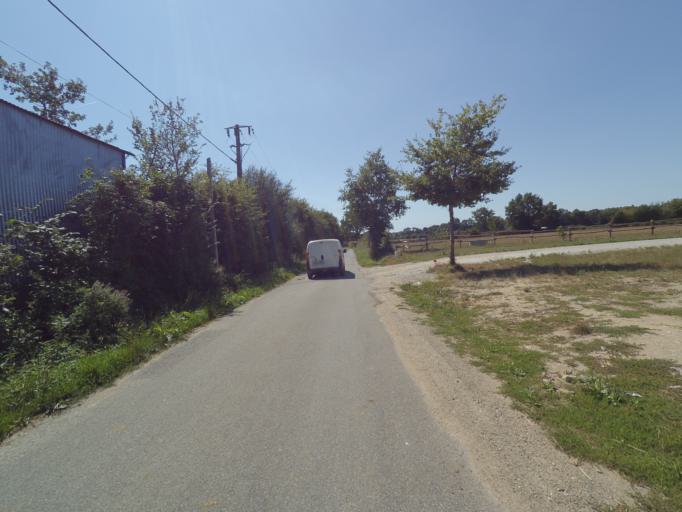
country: FR
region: Pays de la Loire
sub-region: Departement de la Loire-Atlantique
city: Vieillevigne
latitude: 46.9910
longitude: -1.4187
